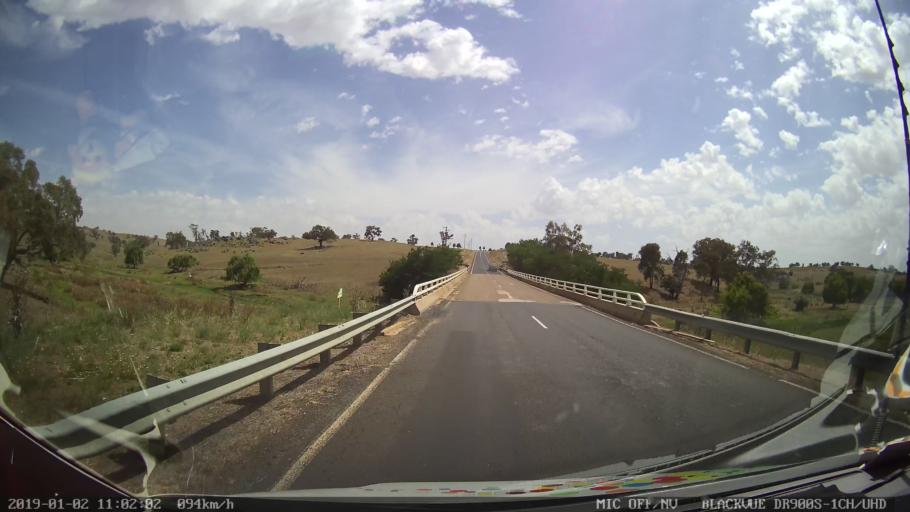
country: AU
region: New South Wales
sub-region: Young
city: Young
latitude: -34.5905
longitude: 148.3241
